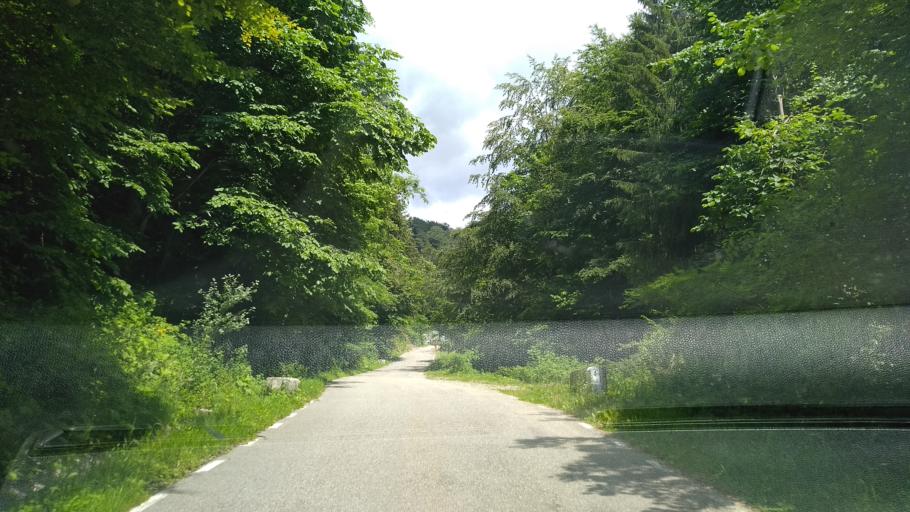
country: RO
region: Hunedoara
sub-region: Comuna Orastioara de Sus
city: Orastioara de Sus
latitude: 45.6233
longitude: 23.3045
